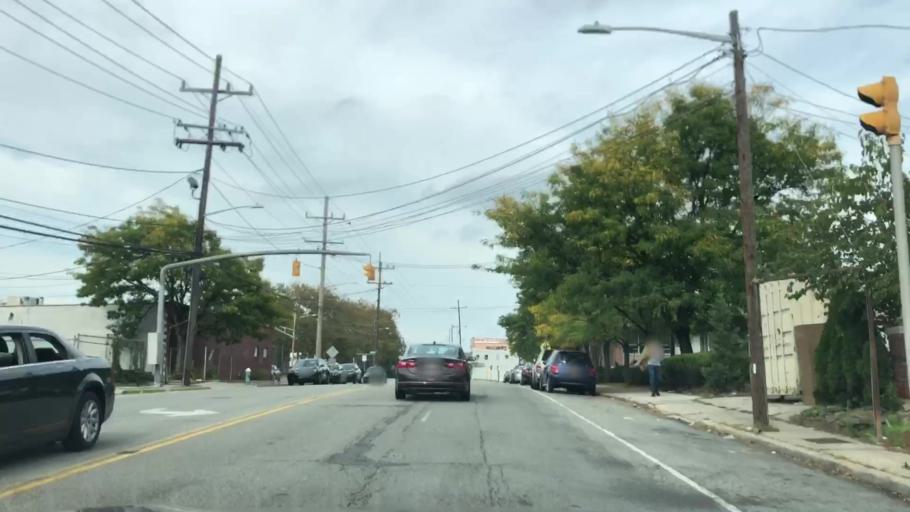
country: US
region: New York
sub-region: Nassau County
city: Elmont
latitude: 40.7088
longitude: -73.7096
